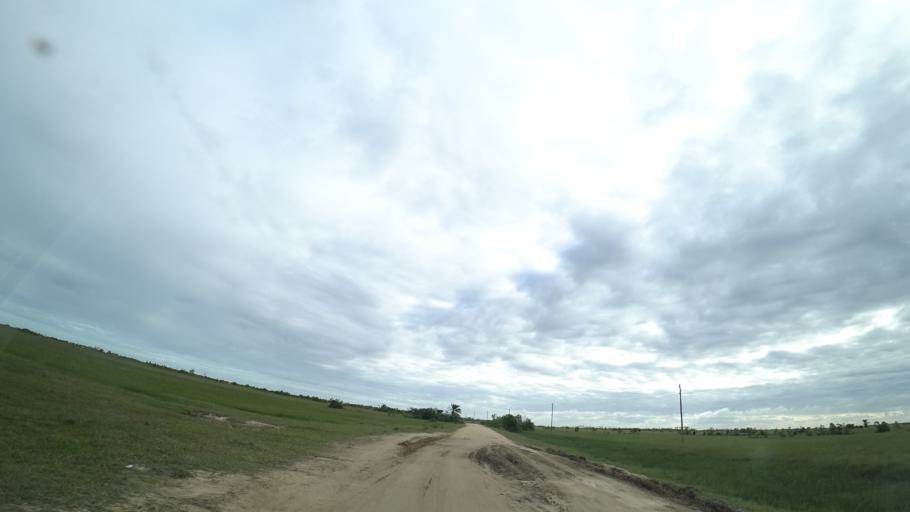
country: MZ
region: Sofala
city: Beira
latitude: -19.7291
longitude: 34.9840
